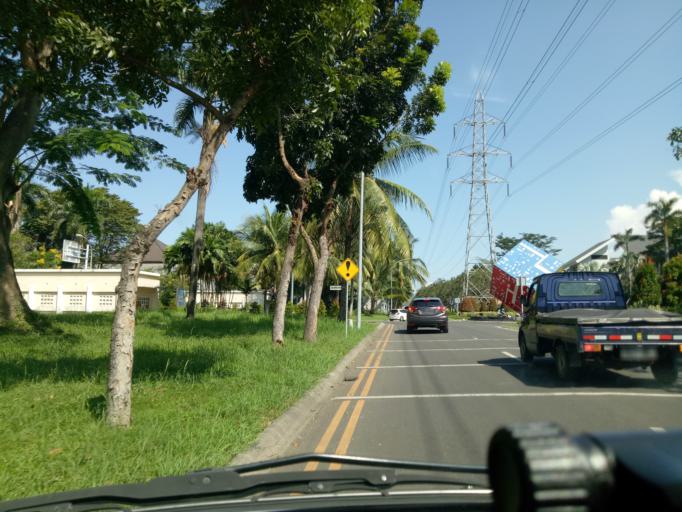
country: ID
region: East Java
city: Driyorejo
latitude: -7.2880
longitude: 112.6478
